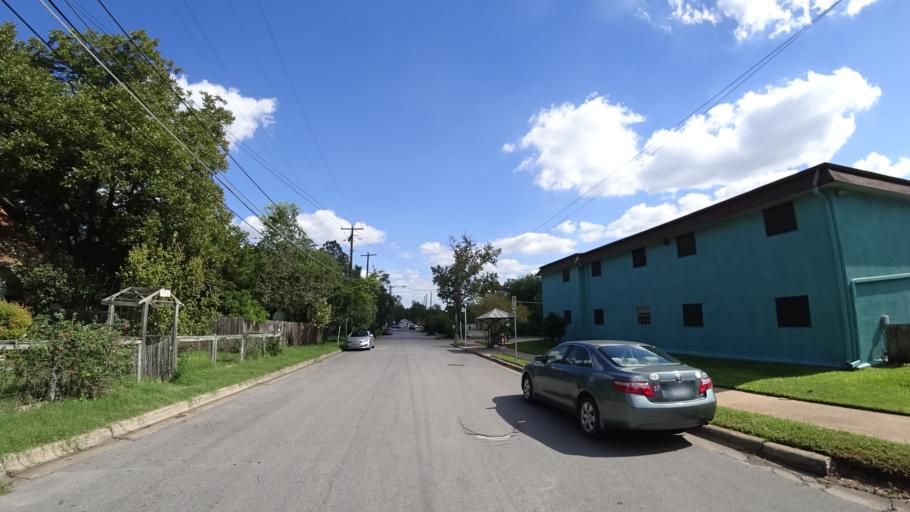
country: US
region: Texas
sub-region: Travis County
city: Austin
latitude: 30.3056
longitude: -97.7174
